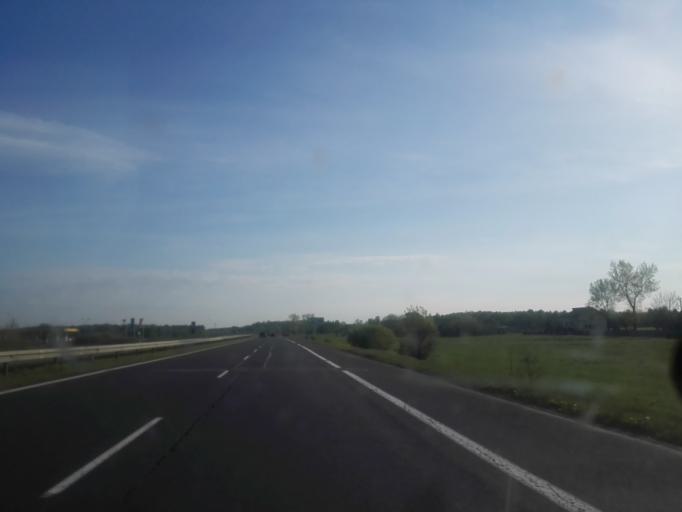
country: PL
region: Lodz Voivodeship
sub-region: Powiat radomszczanski
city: Kamiensk
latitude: 51.2319
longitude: 19.5132
